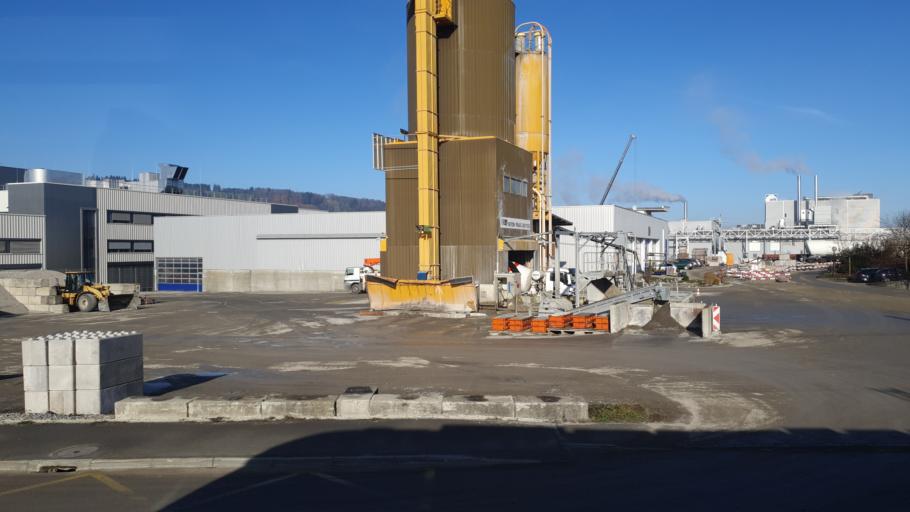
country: CH
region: Fribourg
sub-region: Gruyere District
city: Bulle
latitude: 46.6214
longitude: 7.0400
